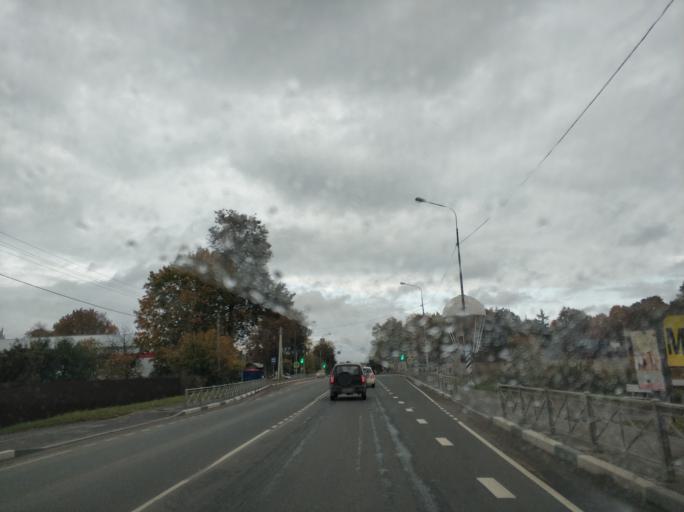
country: RU
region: Pskov
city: Pskov
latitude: 57.7474
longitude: 28.3731
